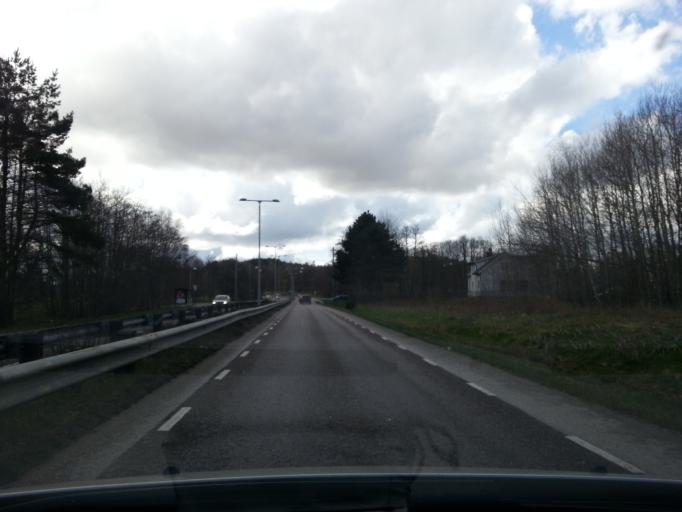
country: SE
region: Vaestra Goetaland
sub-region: Goteborg
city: Goeteborg
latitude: 57.7541
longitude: 11.9397
